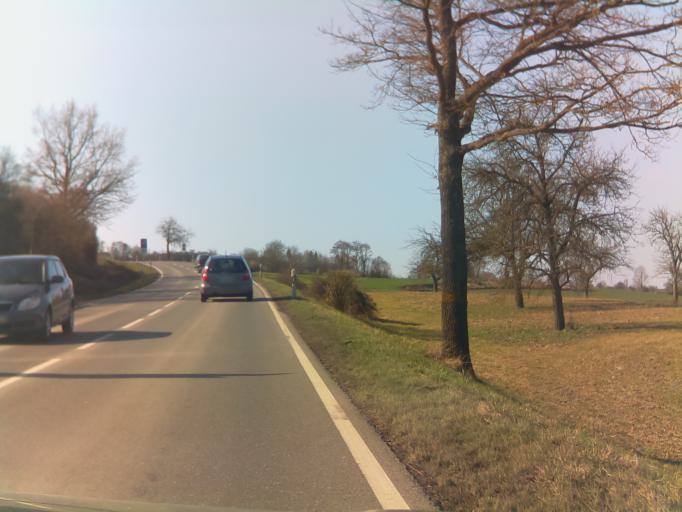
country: DE
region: Baden-Wuerttemberg
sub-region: Karlsruhe Region
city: Horb am Neckar
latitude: 48.4725
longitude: 8.7182
